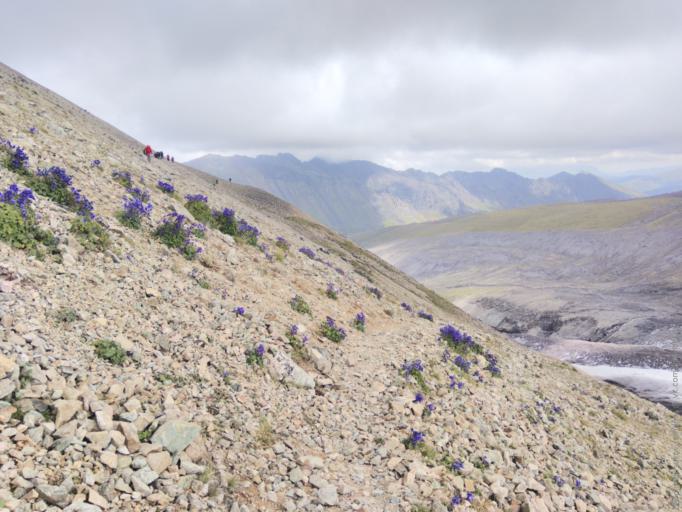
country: RU
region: Kabardino-Balkariya
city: Terskol
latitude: 43.4036
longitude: 42.4204
